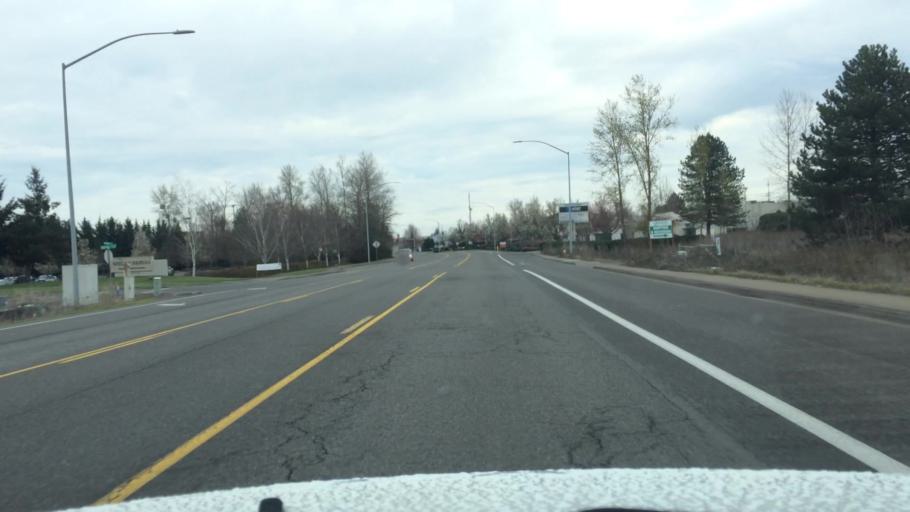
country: US
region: Oregon
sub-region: Marion County
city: Four Corners
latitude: 44.9249
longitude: -122.9941
